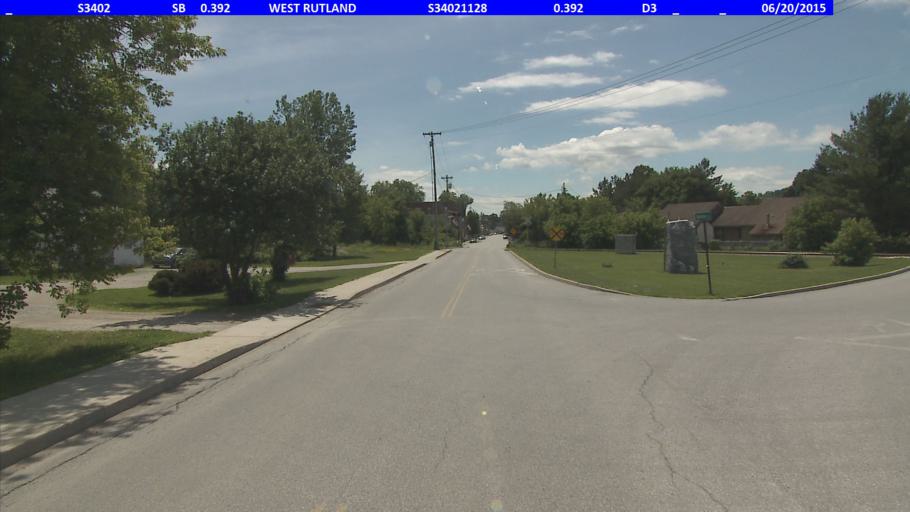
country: US
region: Vermont
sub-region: Rutland County
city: West Rutland
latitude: 43.5998
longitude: -73.0504
